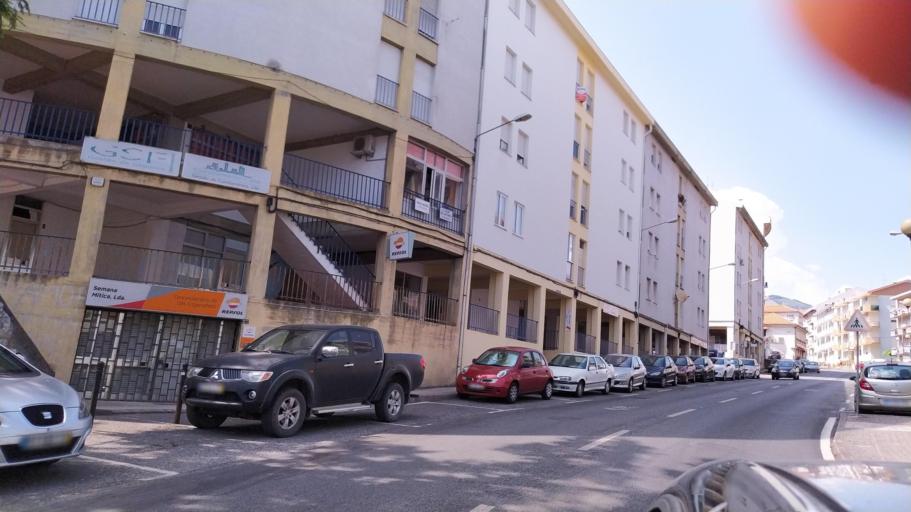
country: PT
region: Castelo Branco
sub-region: Covilha
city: Covilha
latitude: 40.2787
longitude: -7.4983
